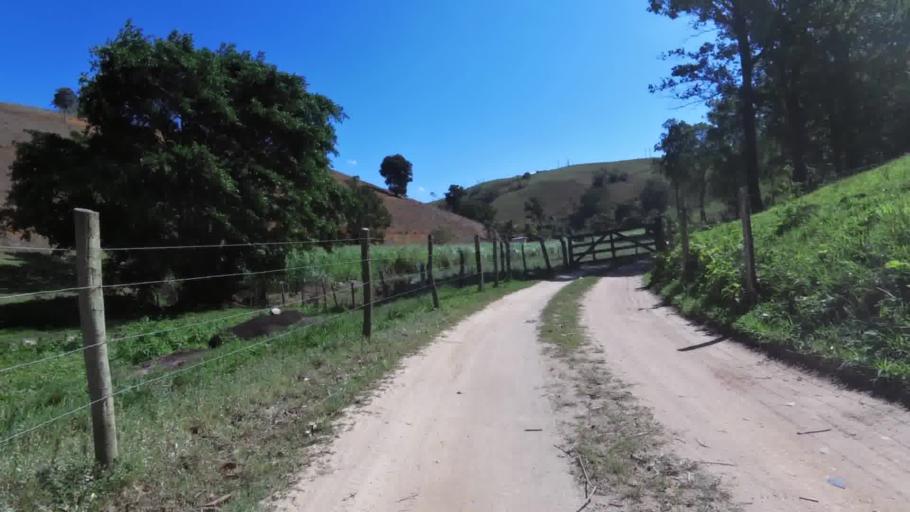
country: BR
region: Espirito Santo
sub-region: Rio Novo Do Sul
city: Rio Novo do Sul
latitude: -20.8717
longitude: -40.9339
